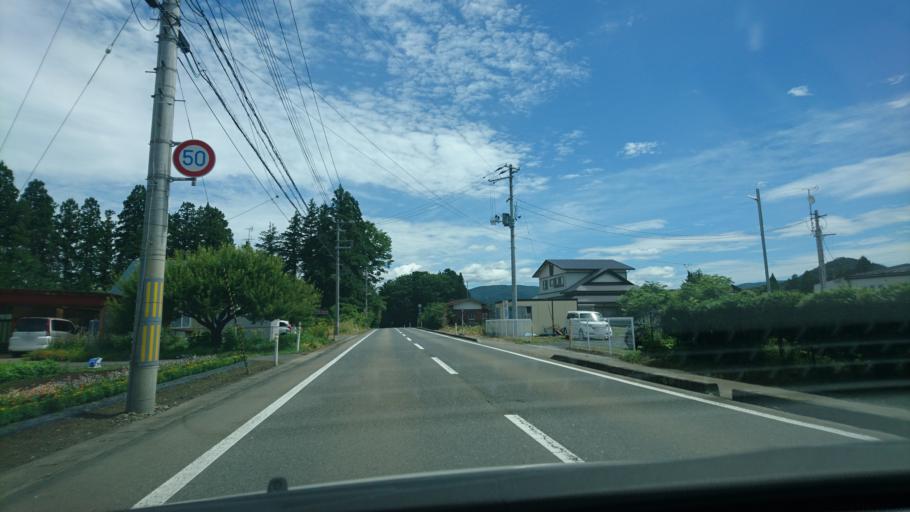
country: JP
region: Iwate
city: Hanamaki
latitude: 39.4119
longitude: 141.1705
